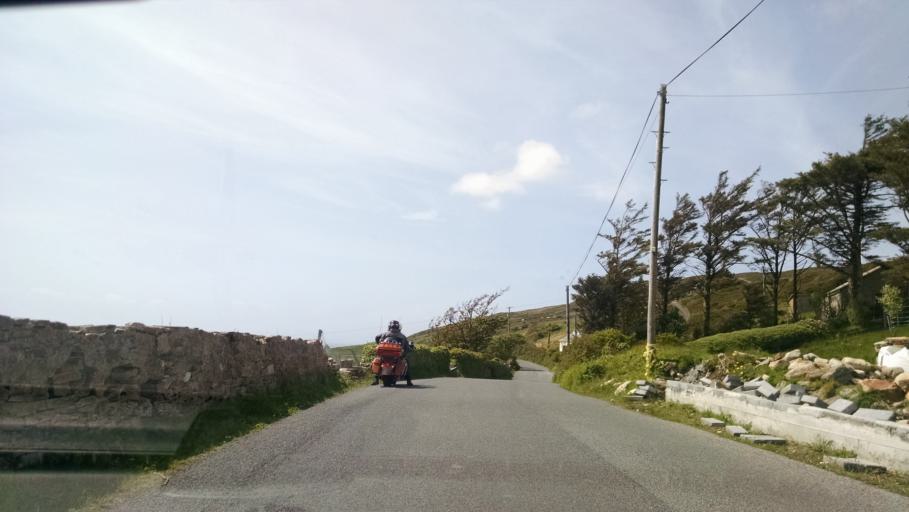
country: IE
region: Connaught
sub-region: County Galway
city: Clifden
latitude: 53.4937
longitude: -10.0543
